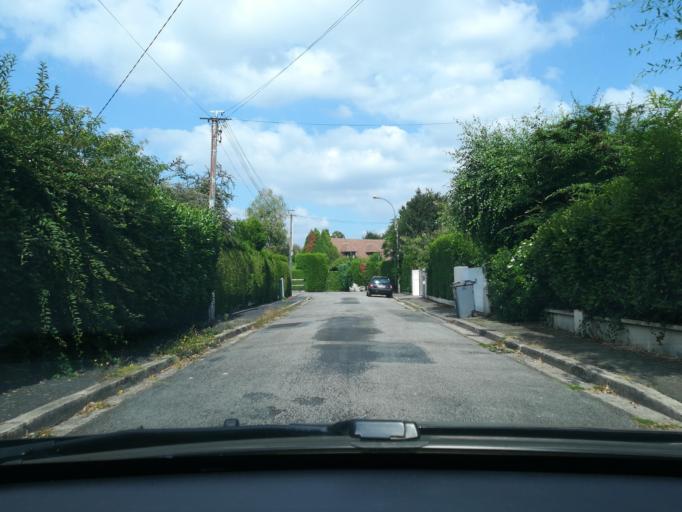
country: FR
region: Haute-Normandie
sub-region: Departement de la Seine-Maritime
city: Bois-Guillaume
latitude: 49.4766
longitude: 1.1184
